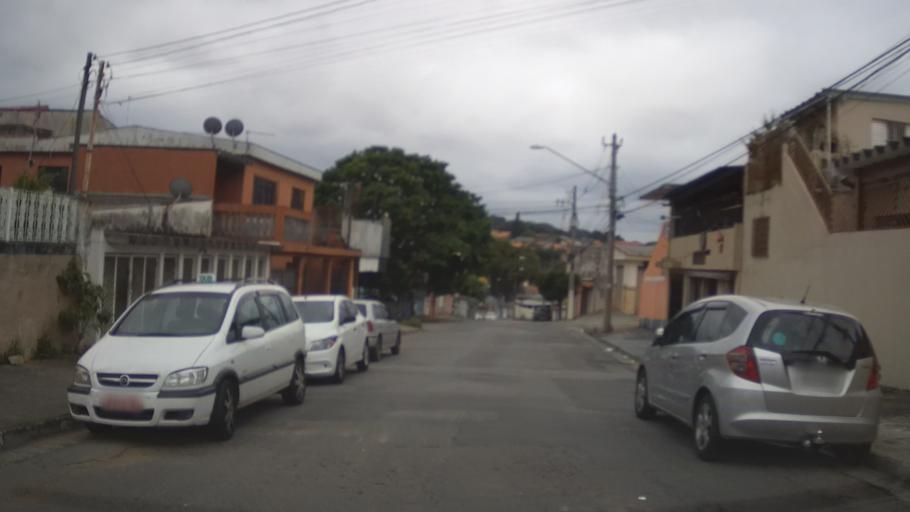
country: BR
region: Sao Paulo
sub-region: Guarulhos
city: Guarulhos
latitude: -23.4459
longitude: -46.5107
